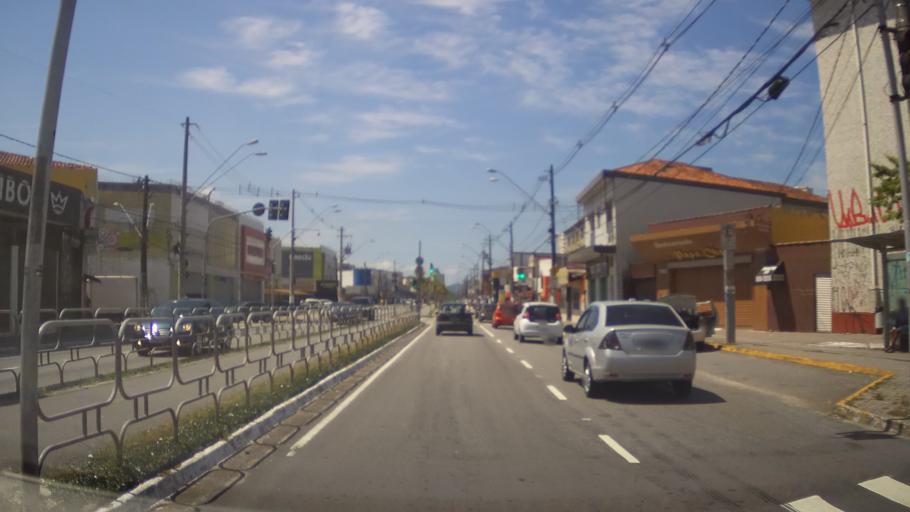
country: BR
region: Sao Paulo
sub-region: Praia Grande
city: Praia Grande
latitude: -24.0257
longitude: -46.4787
